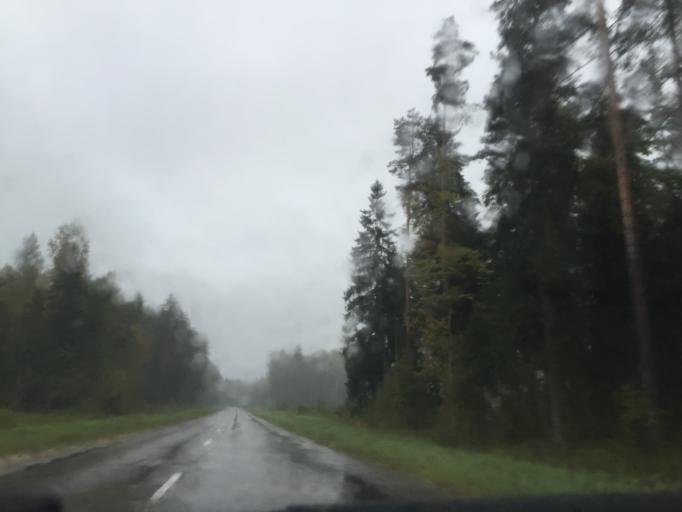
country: LV
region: Ropazu
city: Ropazi
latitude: 57.0153
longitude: 24.6821
